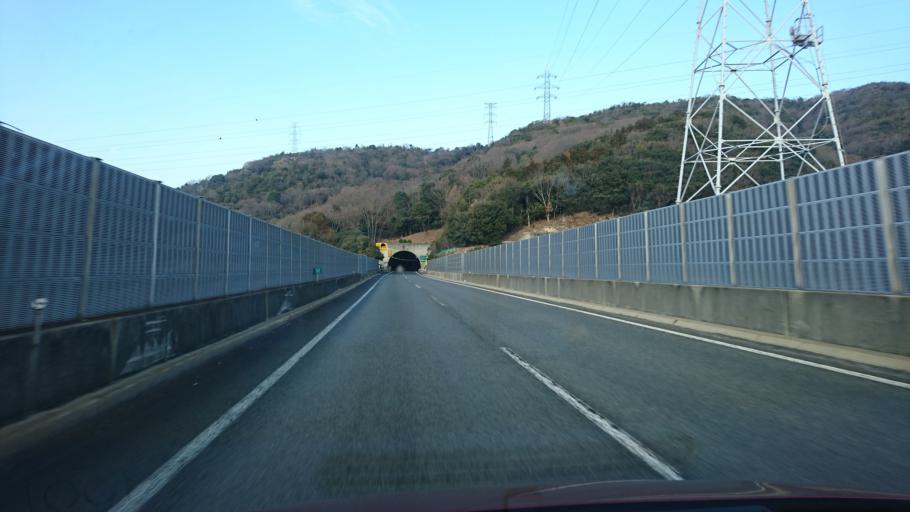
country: JP
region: Hyogo
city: Himeji
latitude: 34.8605
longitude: 134.7204
